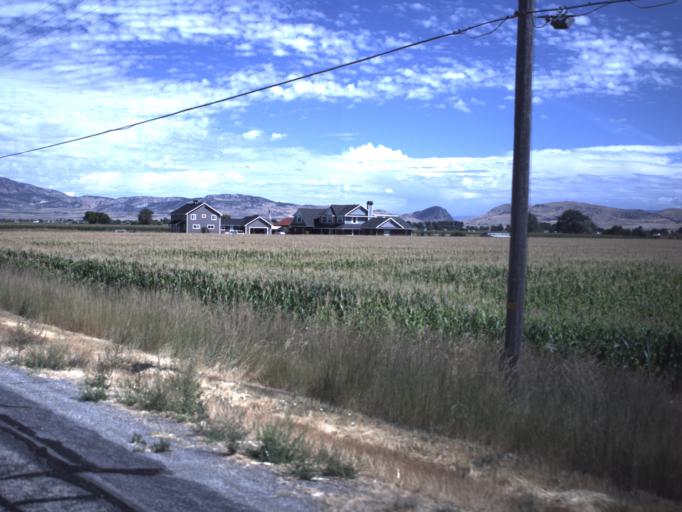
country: US
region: Utah
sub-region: Box Elder County
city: Garland
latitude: 41.7571
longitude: -112.1484
